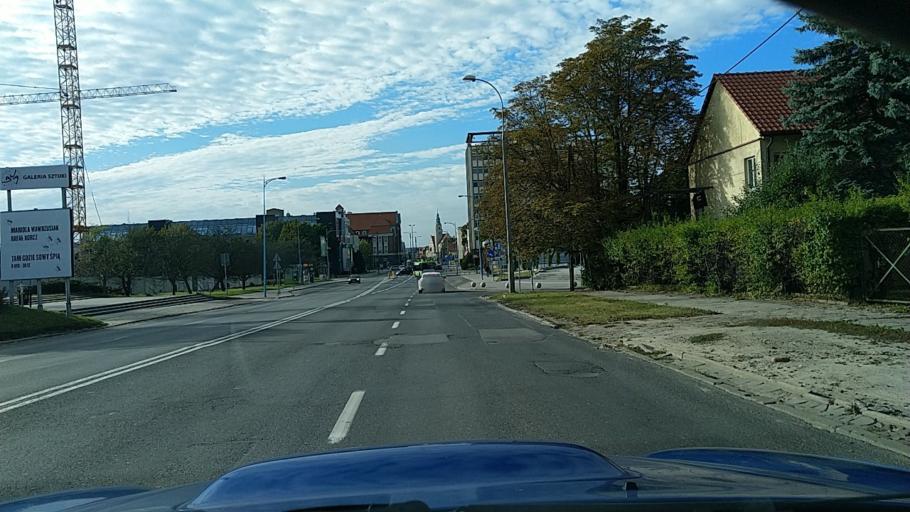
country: PL
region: Warmian-Masurian Voivodeship
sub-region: Powiat olsztynski
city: Olsztyn
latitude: 53.7755
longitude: 20.4914
